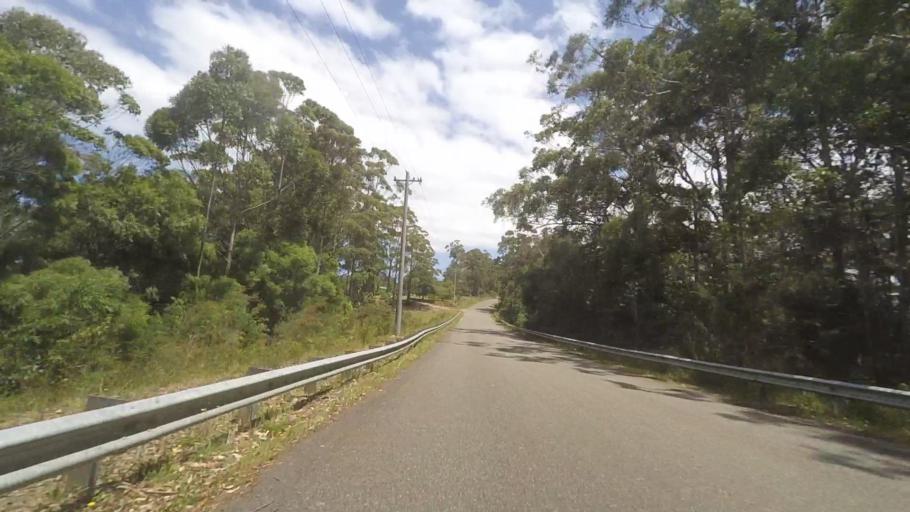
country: AU
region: New South Wales
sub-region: Shoalhaven Shire
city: Milton
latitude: -35.4050
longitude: 150.3600
